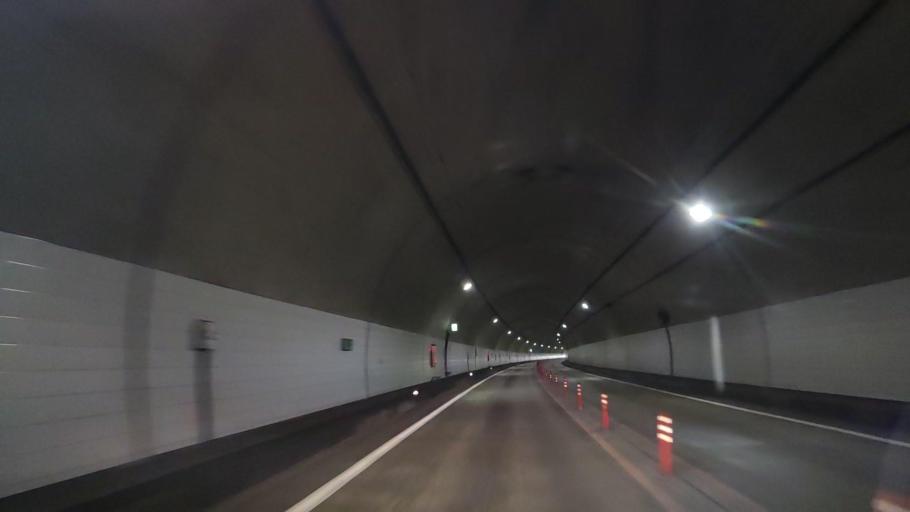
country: JP
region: Akita
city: Odate
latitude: 40.3604
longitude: 140.6943
